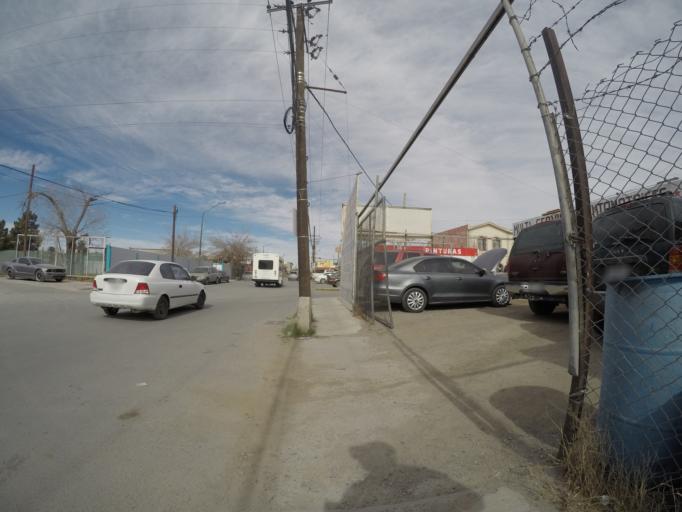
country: MX
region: Chihuahua
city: Ciudad Juarez
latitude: 31.7168
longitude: -106.4325
